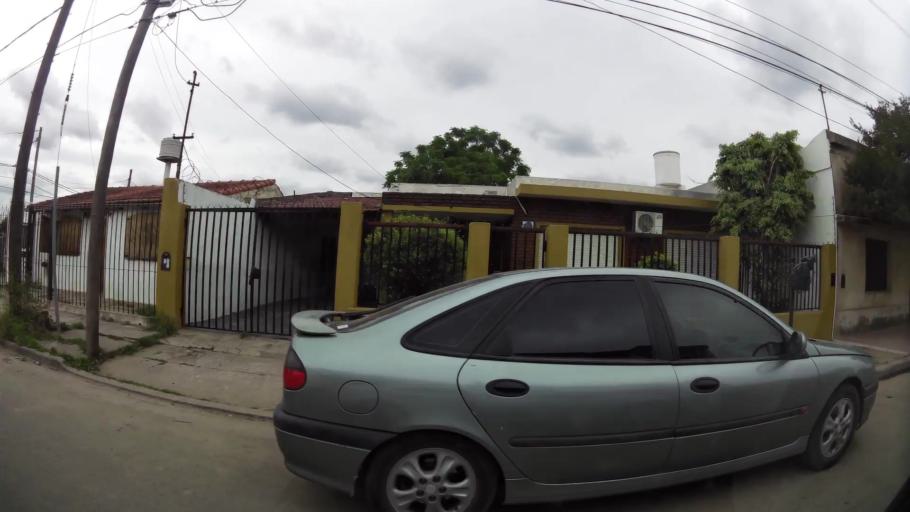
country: AR
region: Buenos Aires
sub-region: Partido de Zarate
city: Zarate
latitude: -34.1107
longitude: -59.0174
